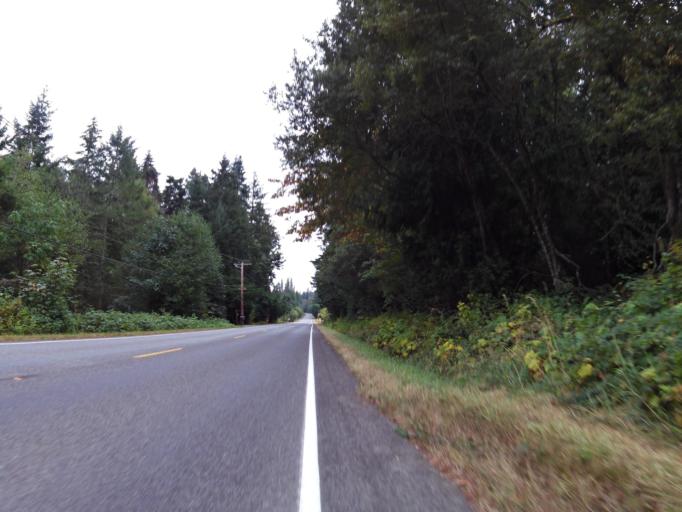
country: US
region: Washington
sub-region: Jefferson County
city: Port Hadlock-Irondale
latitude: 47.9939
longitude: -122.7228
